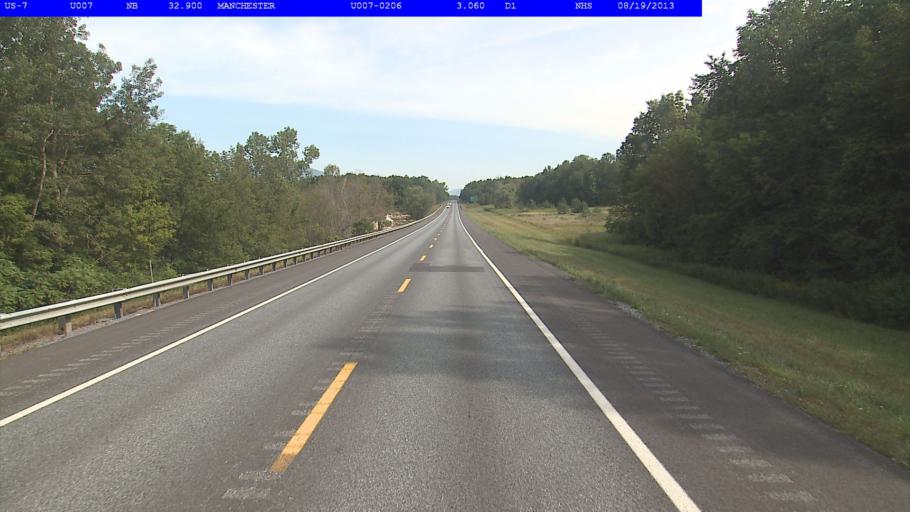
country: US
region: Vermont
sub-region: Bennington County
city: Manchester Center
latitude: 43.1535
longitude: -73.0456
